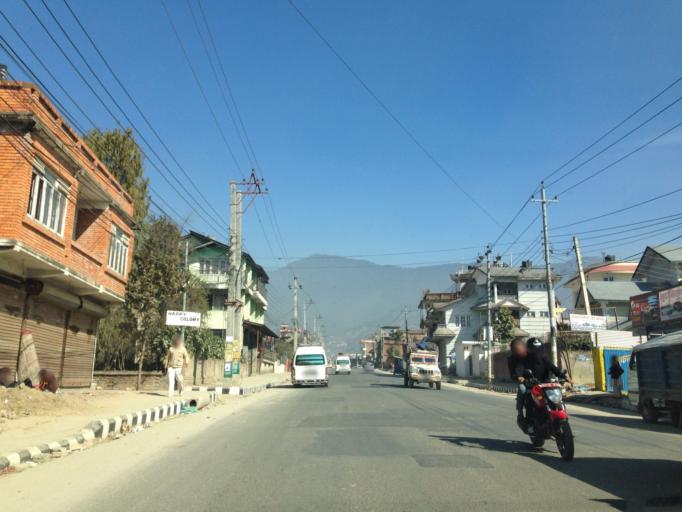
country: NP
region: Central Region
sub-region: Bagmati Zone
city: Kathmandu
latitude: 27.7586
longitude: 85.3505
